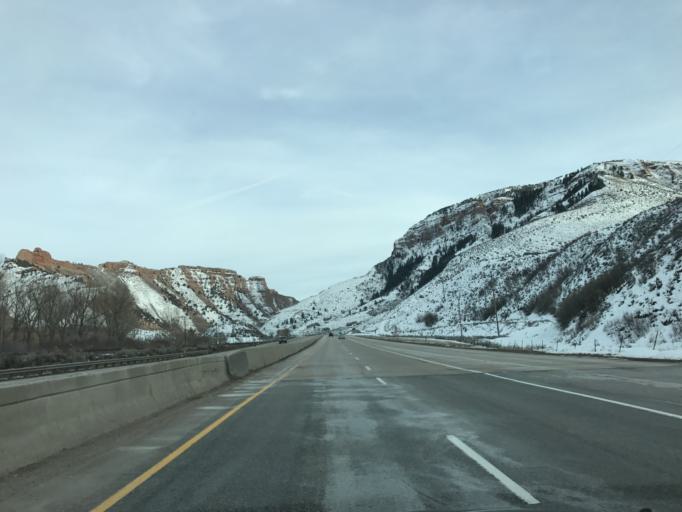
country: US
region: Utah
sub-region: Morgan County
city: Morgan
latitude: 41.0633
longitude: -111.5465
